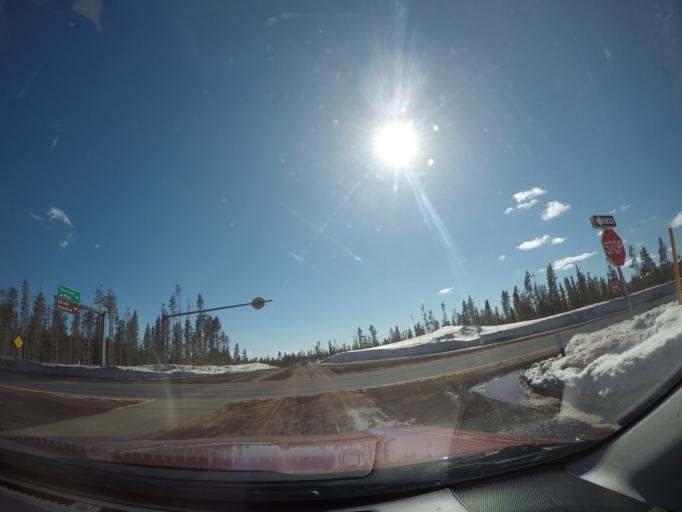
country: US
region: Oregon
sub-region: Deschutes County
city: Sunriver
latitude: 43.9821
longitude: -121.6136
